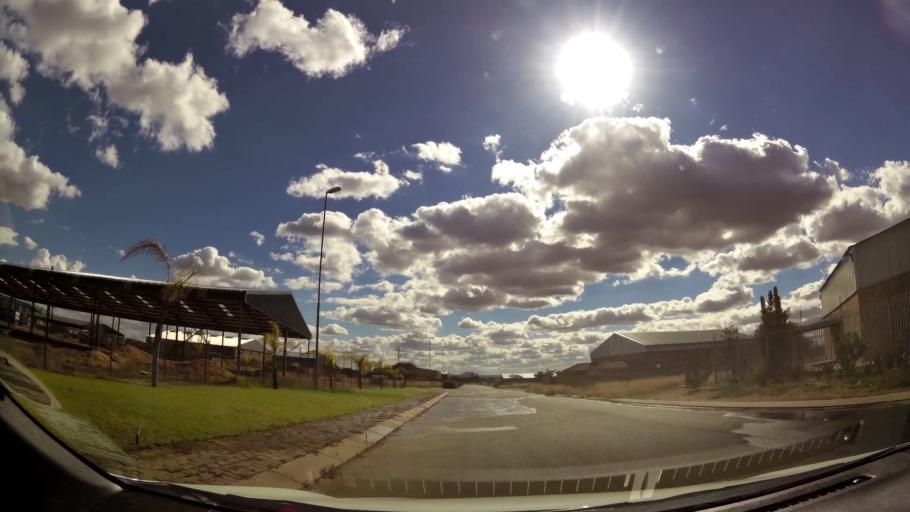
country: ZA
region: Limpopo
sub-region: Capricorn District Municipality
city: Polokwane
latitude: -23.8647
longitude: 29.4807
